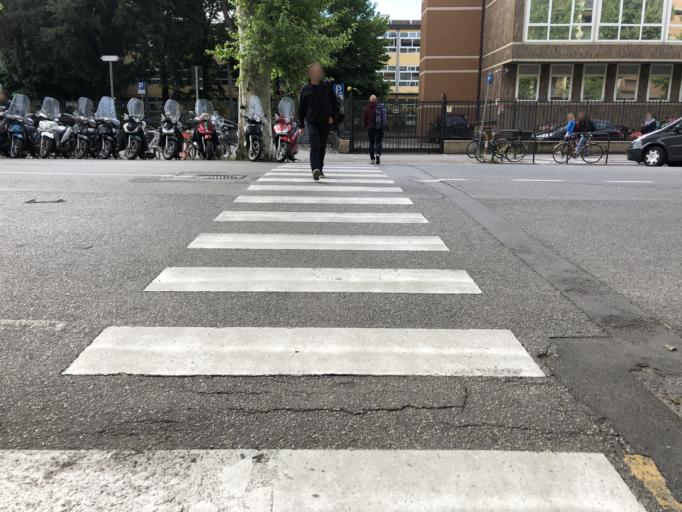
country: IT
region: Tuscany
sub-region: Province of Florence
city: Florence
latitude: 43.7769
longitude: 11.2765
